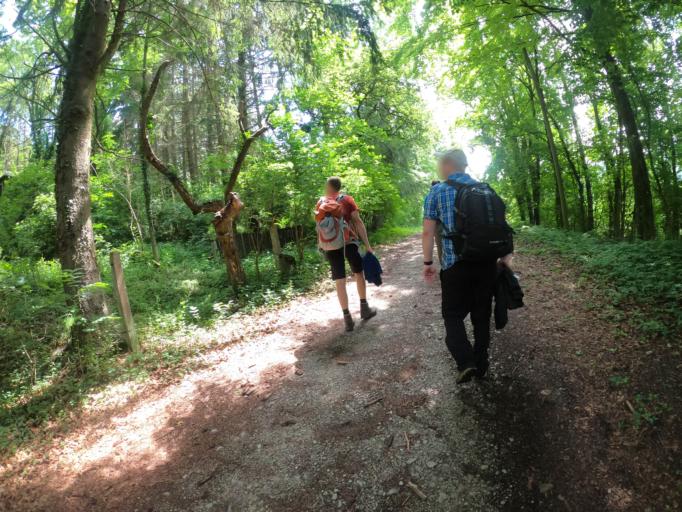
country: DE
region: Bavaria
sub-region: Upper Franconia
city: Poxdorf
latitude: 49.9230
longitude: 11.0723
